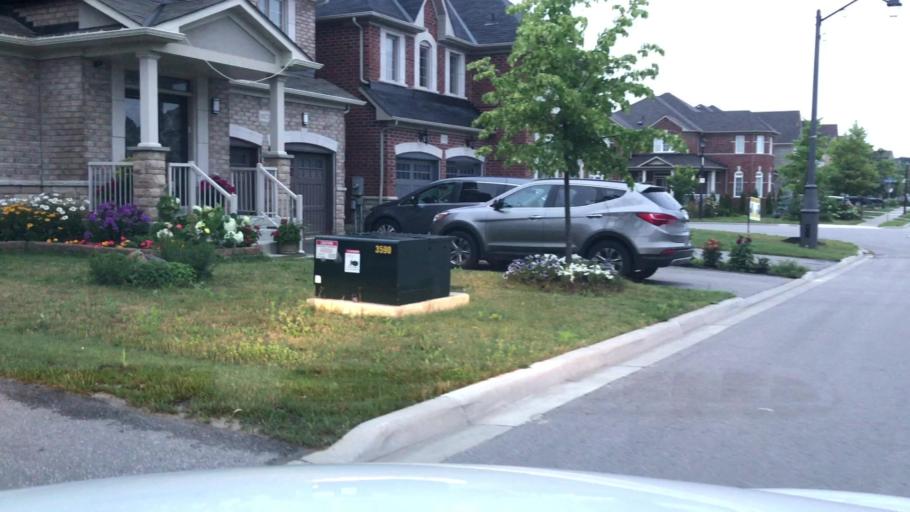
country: CA
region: Ontario
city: Newmarket
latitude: 44.0372
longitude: -79.4222
